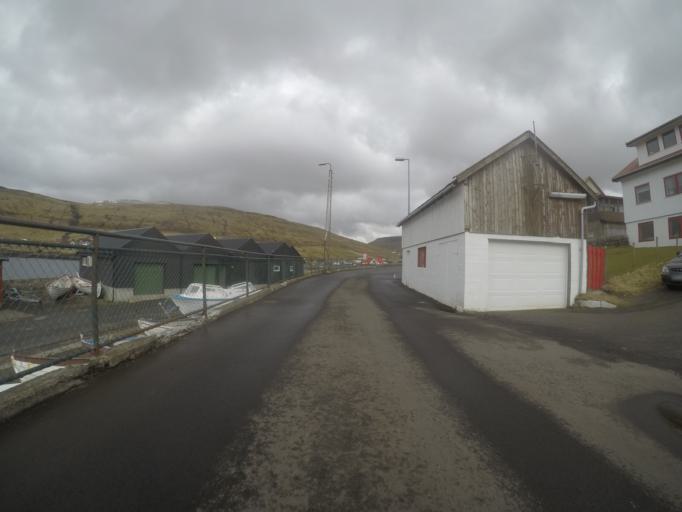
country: FO
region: Vagar
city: Midvagur
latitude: 62.0511
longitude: -7.1513
